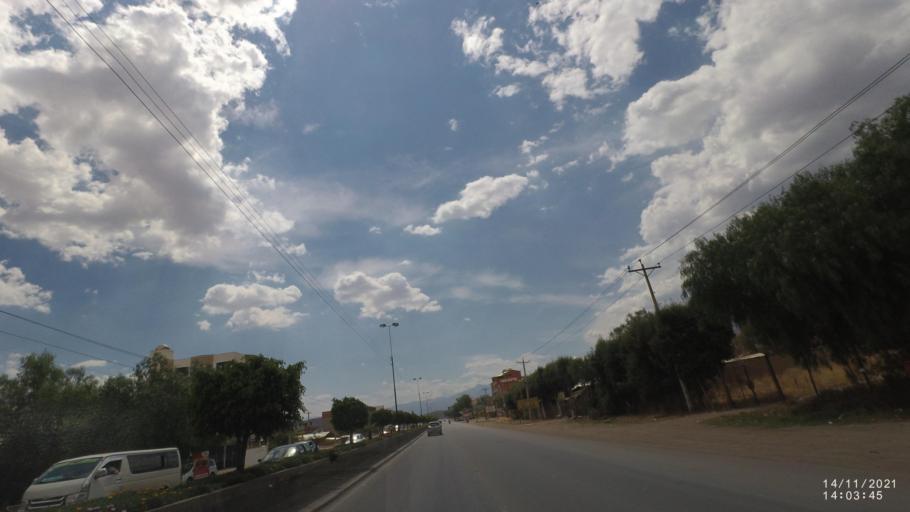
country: BO
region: Cochabamba
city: Cochabamba
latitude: -17.3853
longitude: -66.1021
